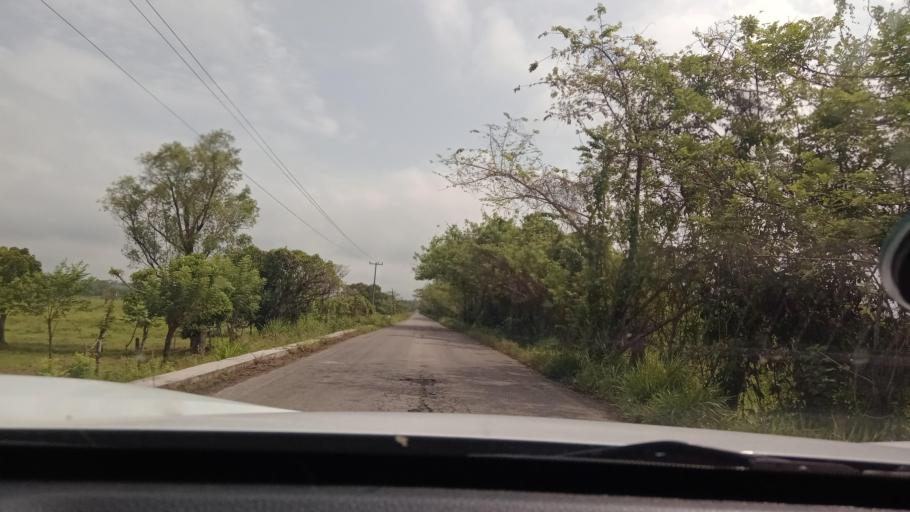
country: MX
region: Tabasco
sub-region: Huimanguillo
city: Francisco Rueda
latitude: 17.5563
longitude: -94.1209
